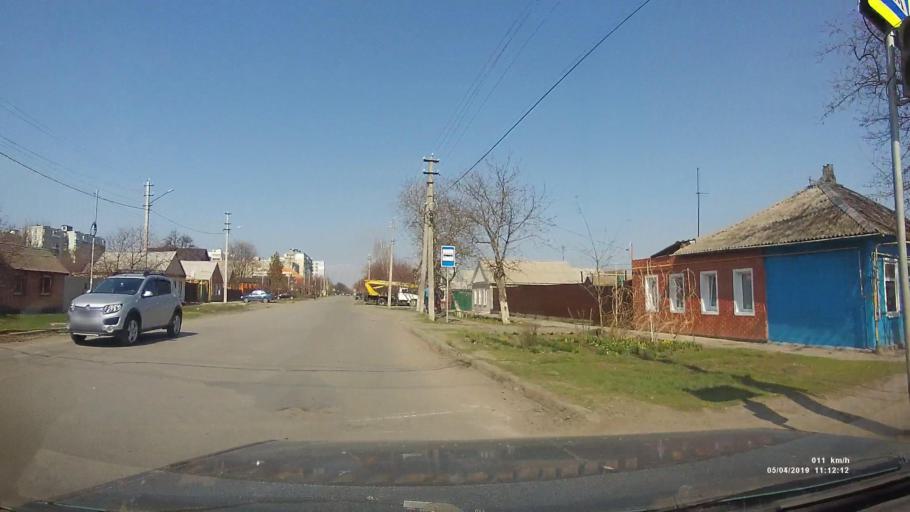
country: RU
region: Rostov
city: Azov
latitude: 47.0972
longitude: 39.4383
